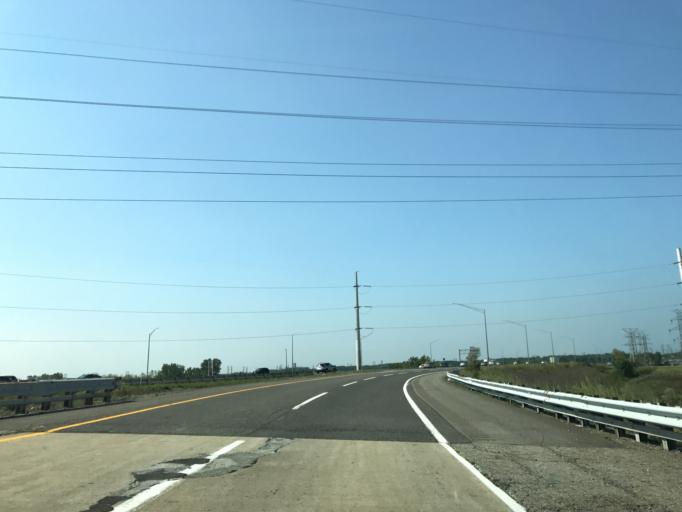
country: US
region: Indiana
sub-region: Lake County
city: Whiting
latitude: 41.6577
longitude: -87.5153
